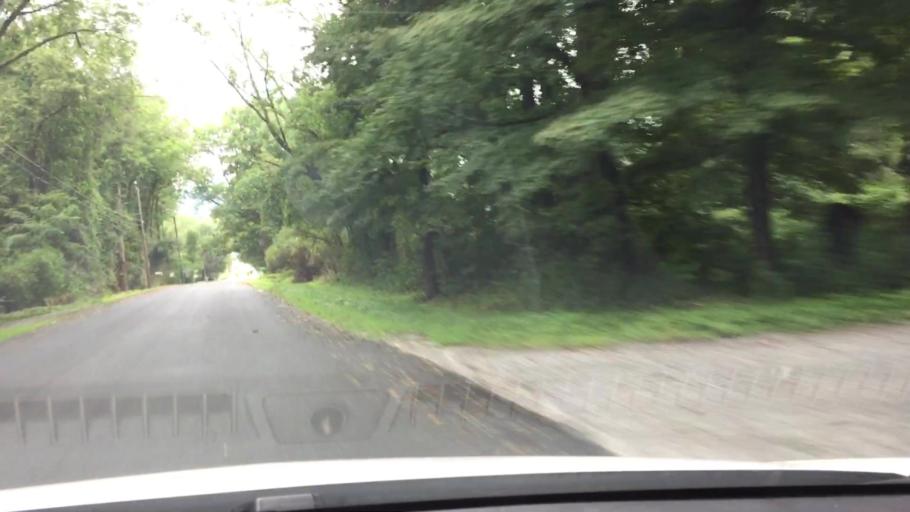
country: US
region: Massachusetts
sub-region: Berkshire County
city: Richmond
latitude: 42.3666
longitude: -73.3681
